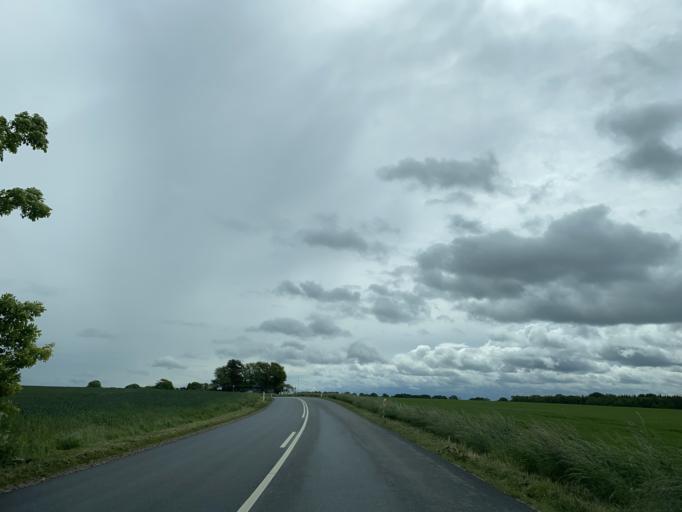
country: DK
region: Central Jutland
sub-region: Arhus Kommune
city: Sabro
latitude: 56.2502
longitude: 9.9926
